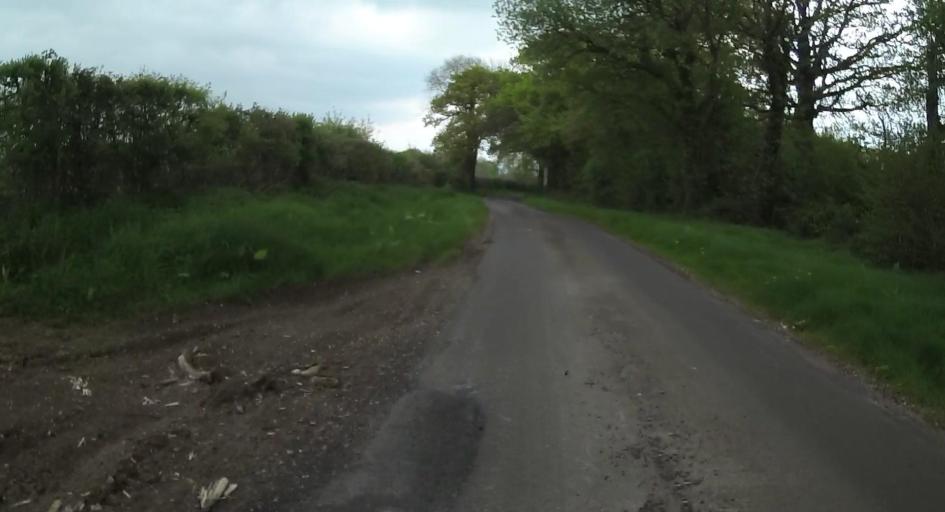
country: GB
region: England
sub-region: Hampshire
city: Long Sutton
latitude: 51.1866
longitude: -0.9406
